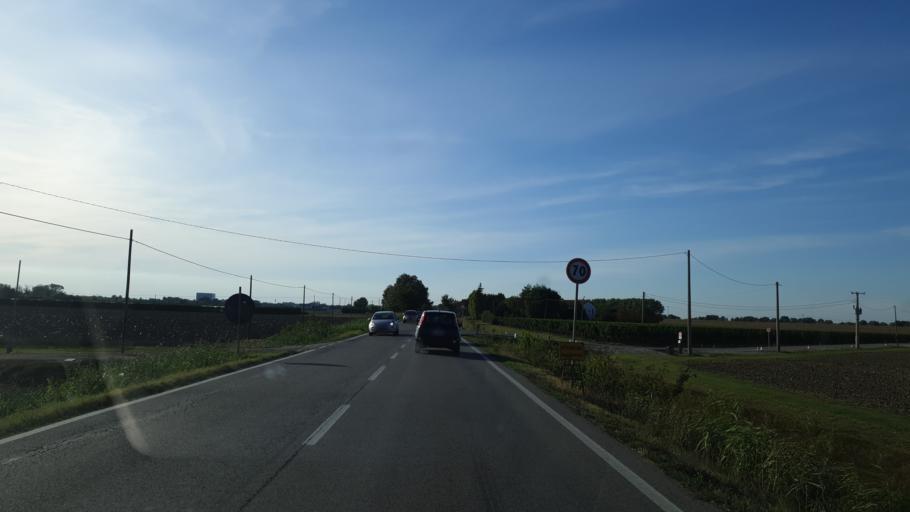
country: IT
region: Emilia-Romagna
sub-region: Provincia di Ravenna
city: Lavezzola
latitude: 44.5648
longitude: 11.9008
